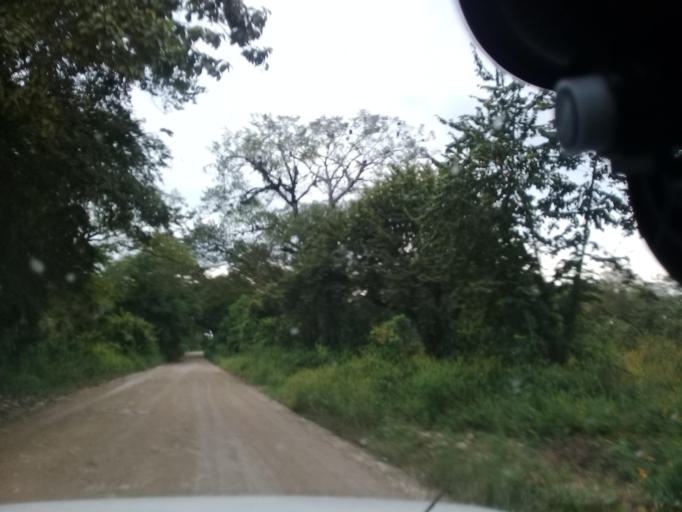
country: MX
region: Hidalgo
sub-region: Huejutla de Reyes
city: Chalahuiyapa
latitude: 21.1569
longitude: -98.3730
